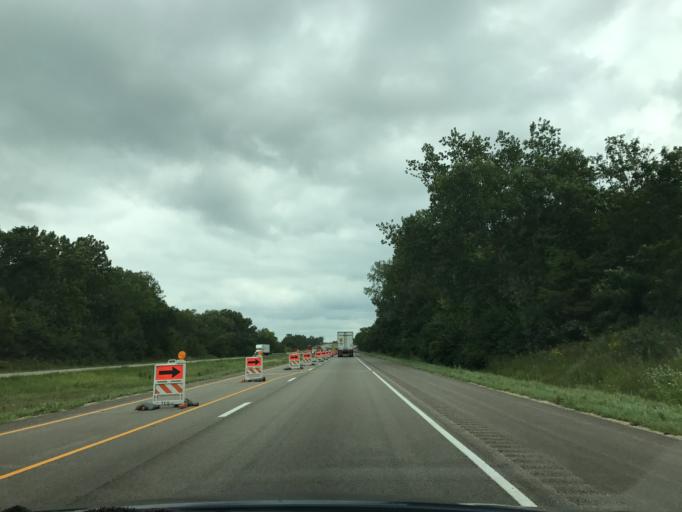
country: US
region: Illinois
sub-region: Bureau County
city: Princeton
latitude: 41.3945
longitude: -89.5787
